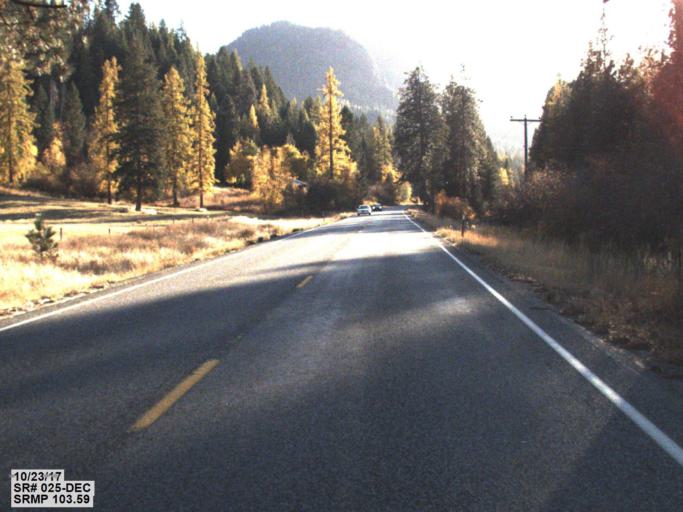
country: US
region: Washington
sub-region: Stevens County
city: Kettle Falls
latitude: 48.8230
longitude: -117.9159
